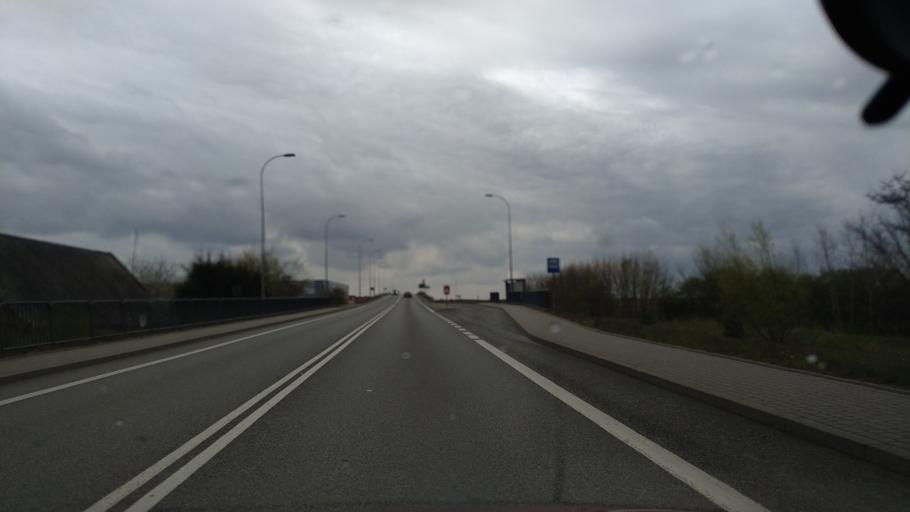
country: PL
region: Pomeranian Voivodeship
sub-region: Powiat tczewski
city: Subkowy
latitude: 54.0375
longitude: 18.6661
